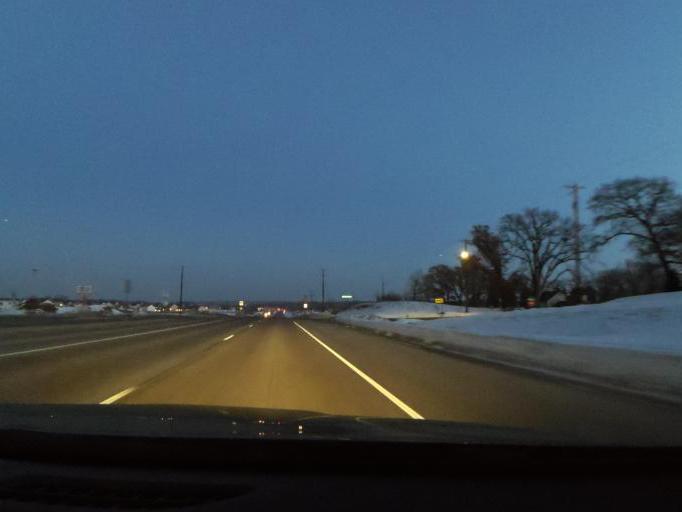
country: US
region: Minnesota
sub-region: Scott County
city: Prior Lake
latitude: 44.7174
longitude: -93.3911
